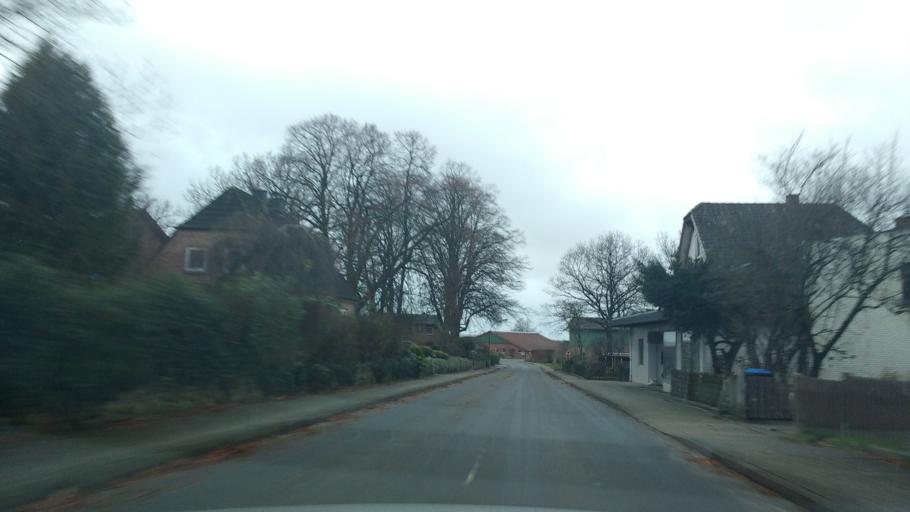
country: DE
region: Schleswig-Holstein
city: Nindorf
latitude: 54.1321
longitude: 9.6981
